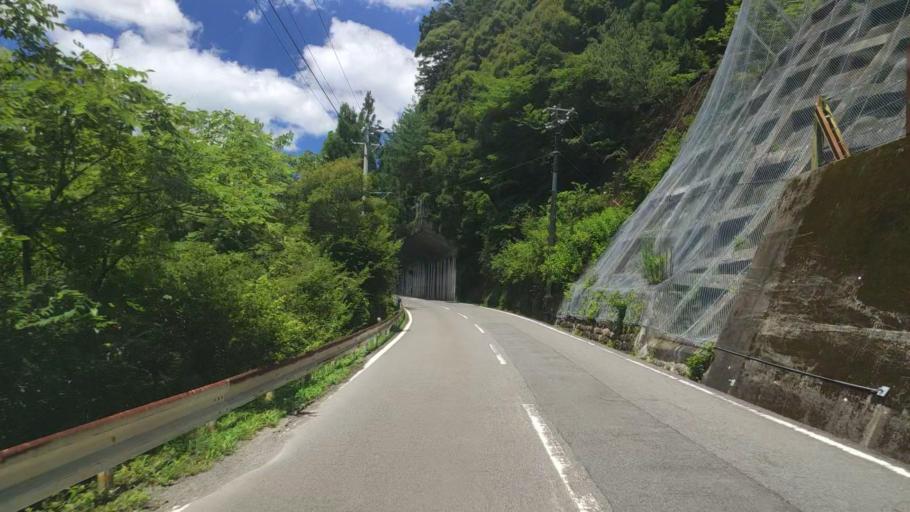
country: JP
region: Mie
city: Owase
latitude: 33.9974
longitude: 136.0123
